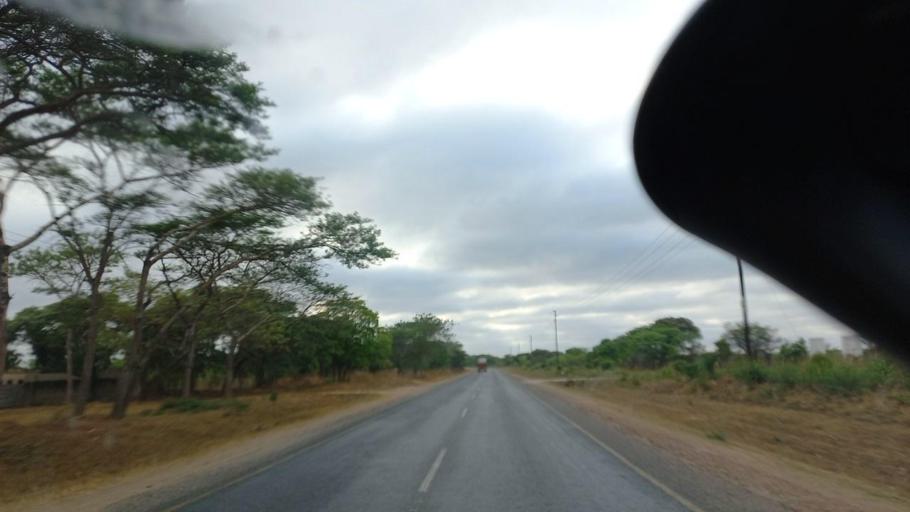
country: ZM
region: Lusaka
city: Chongwe
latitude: -15.3507
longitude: 28.5375
